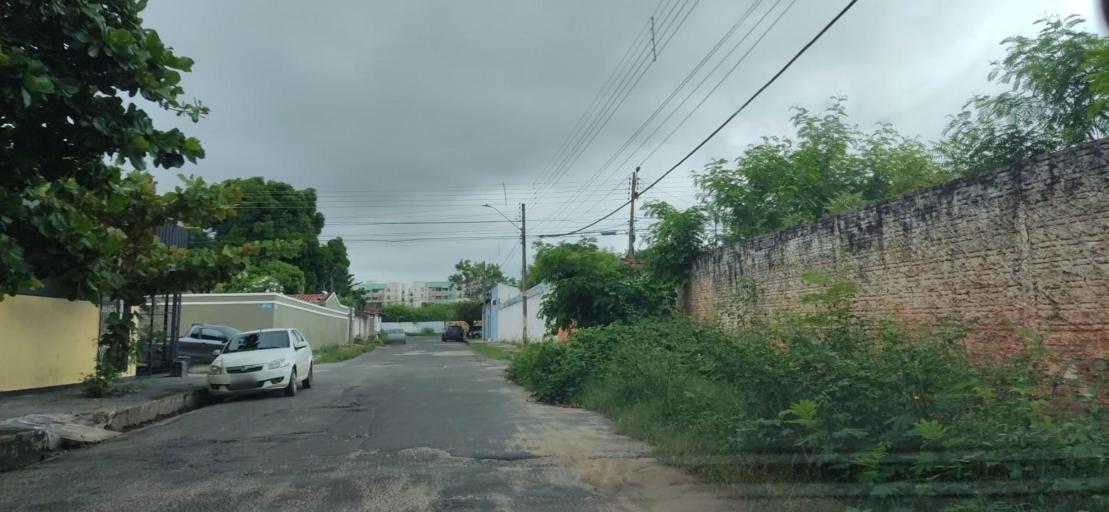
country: BR
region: Piaui
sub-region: Teresina
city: Teresina
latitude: -5.0712
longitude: -42.7561
